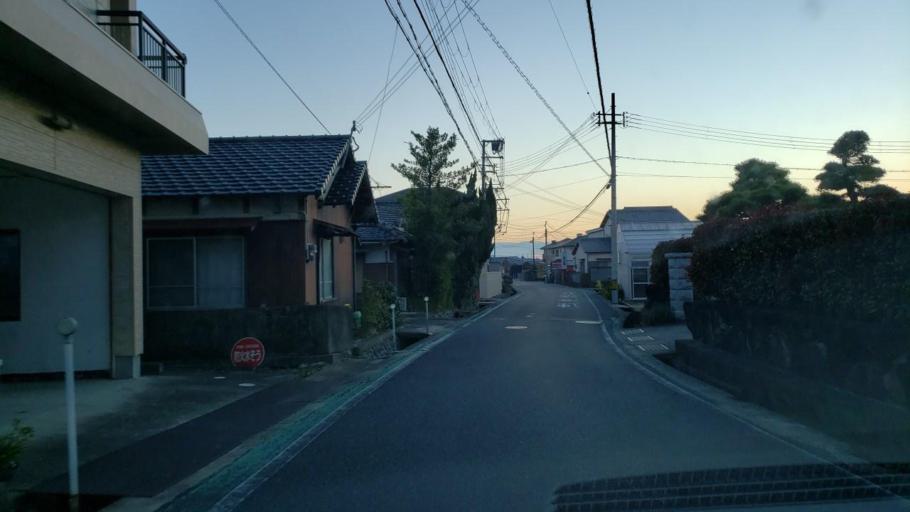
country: JP
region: Hyogo
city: Fukura
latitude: 34.3045
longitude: 134.7643
